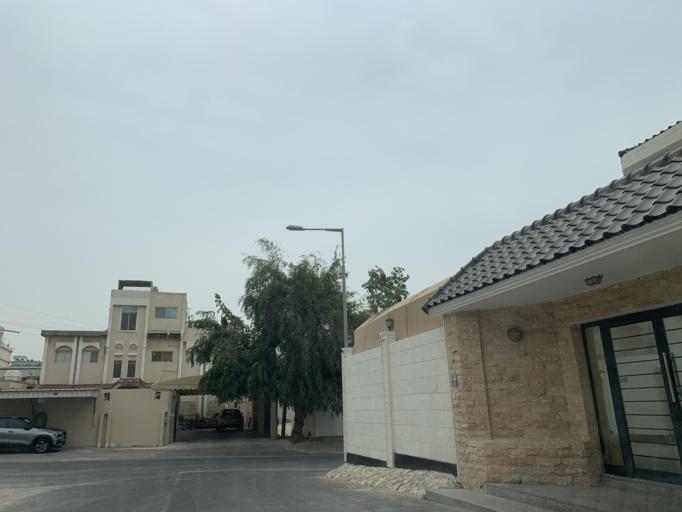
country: BH
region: Northern
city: Ar Rifa'
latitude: 26.1371
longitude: 50.5537
